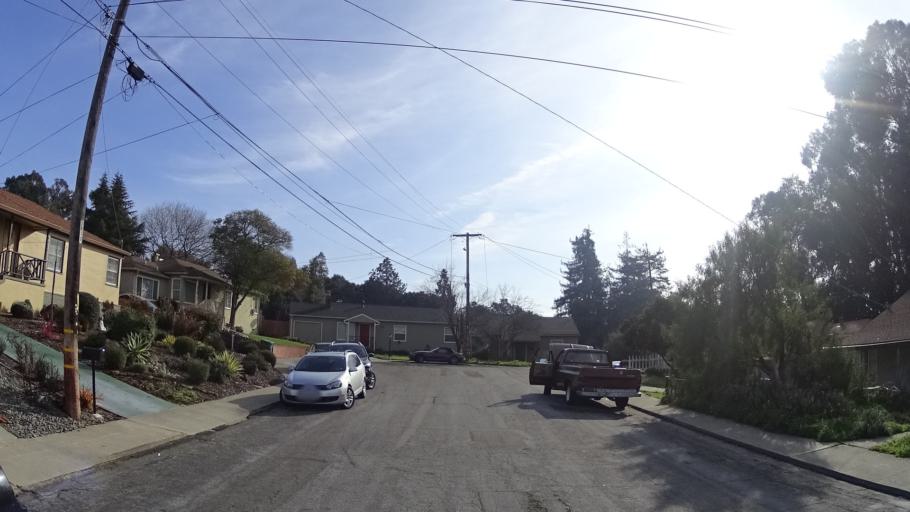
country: US
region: California
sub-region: Alameda County
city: Fairview
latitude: 37.6860
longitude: -122.0572
